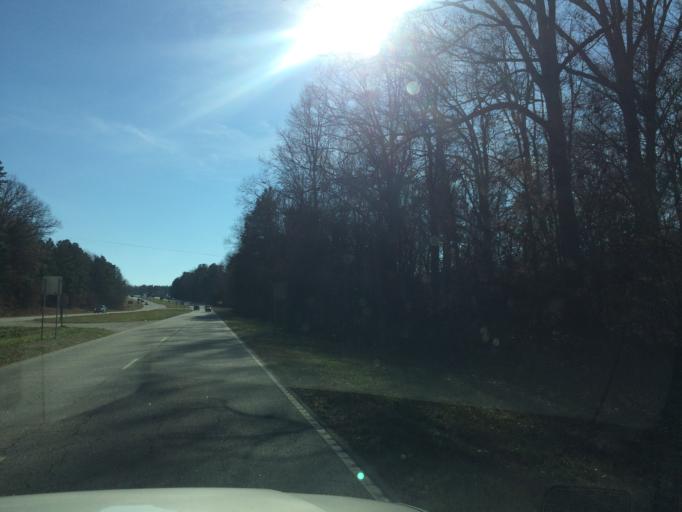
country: US
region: South Carolina
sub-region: Greenwood County
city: Greenwood
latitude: 34.2430
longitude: -82.1009
